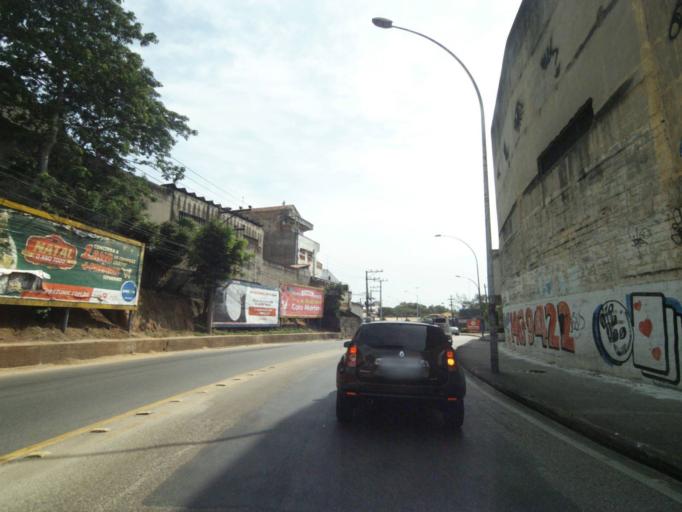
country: BR
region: Rio de Janeiro
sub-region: Rio De Janeiro
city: Rio de Janeiro
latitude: -22.8698
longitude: -43.2487
